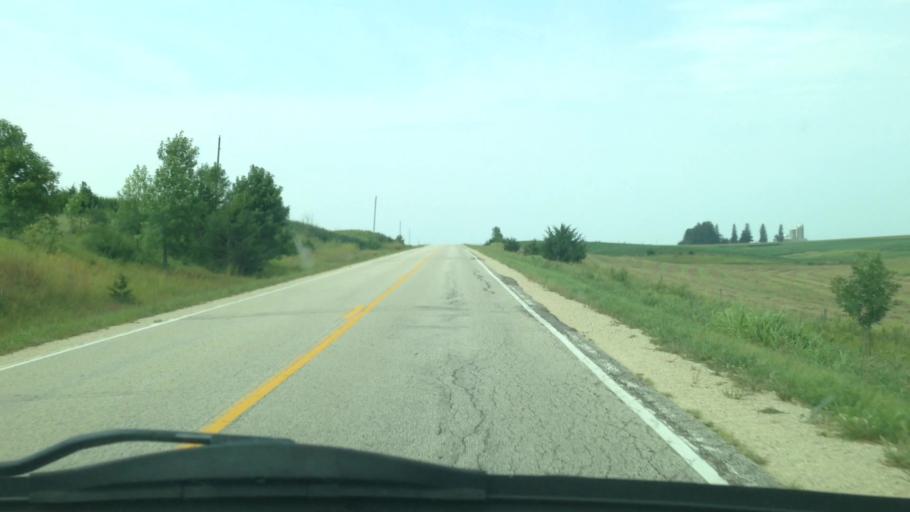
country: US
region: Minnesota
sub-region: Winona County
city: Saint Charles
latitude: 43.8533
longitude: -91.9594
